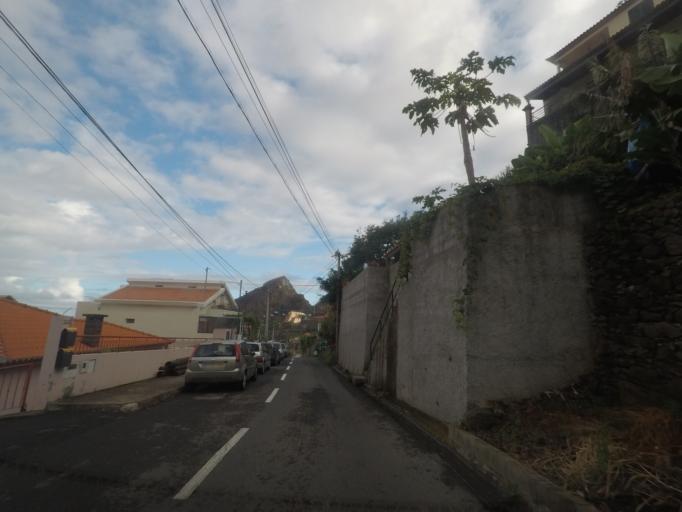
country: PT
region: Madeira
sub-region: Ribeira Brava
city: Campanario
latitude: 32.6593
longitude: -16.9979
